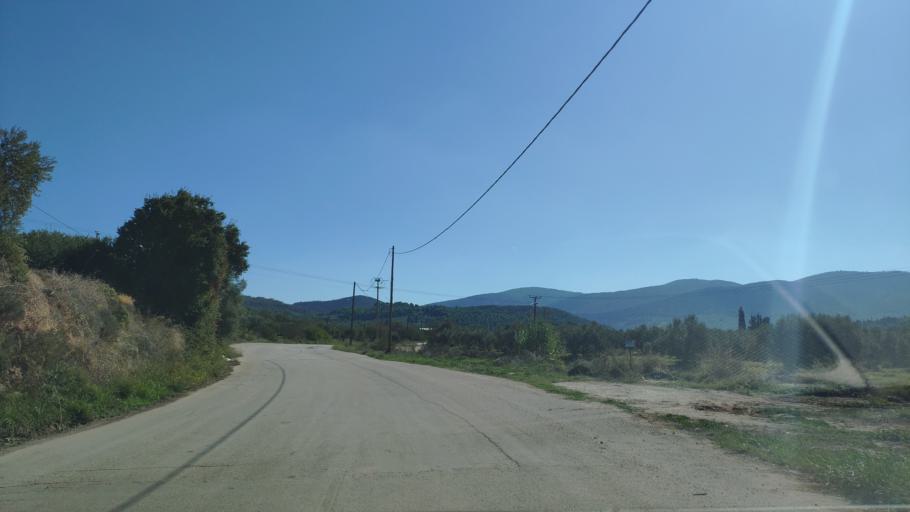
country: GR
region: Peloponnese
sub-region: Nomos Korinthias
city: Athikia
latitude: 37.8408
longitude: 22.9082
